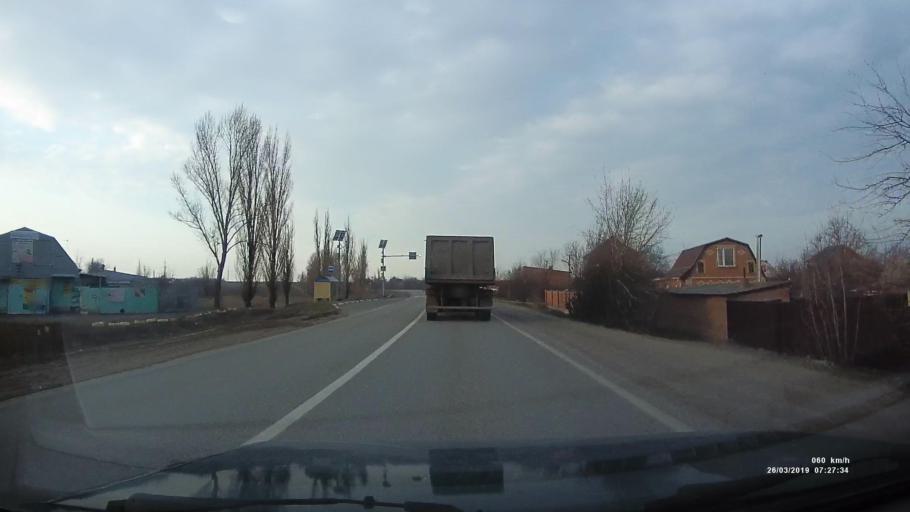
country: RU
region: Rostov
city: Taganrog
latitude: 47.2617
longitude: 38.8273
